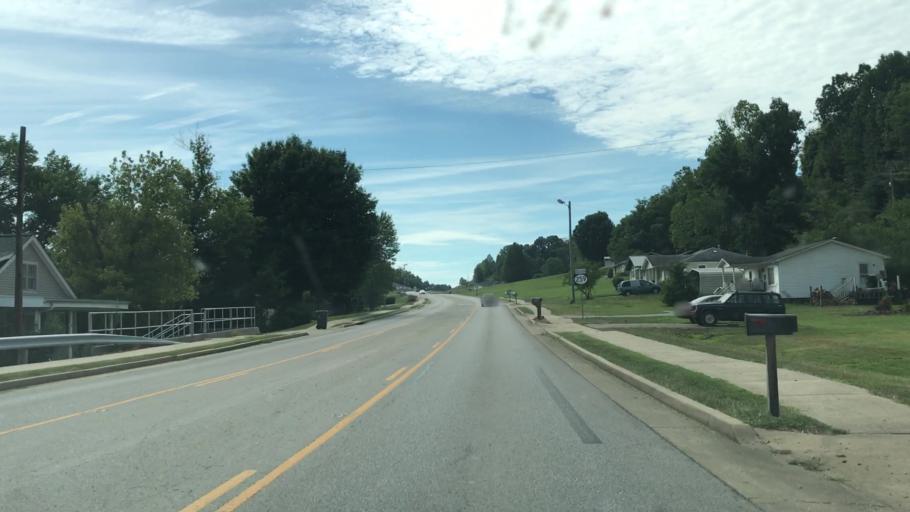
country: US
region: Kentucky
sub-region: Edmonson County
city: Brownsville
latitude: 37.1870
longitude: -86.2518
